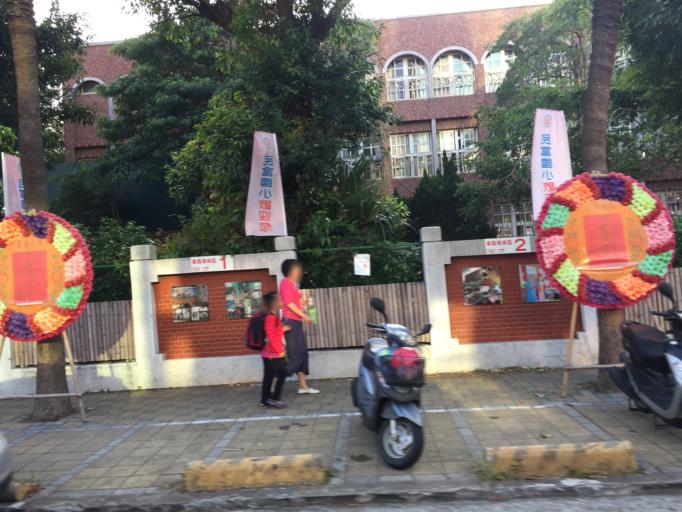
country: TW
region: Taiwan
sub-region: Hsinchu
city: Hsinchu
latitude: 24.8081
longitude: 120.9609
